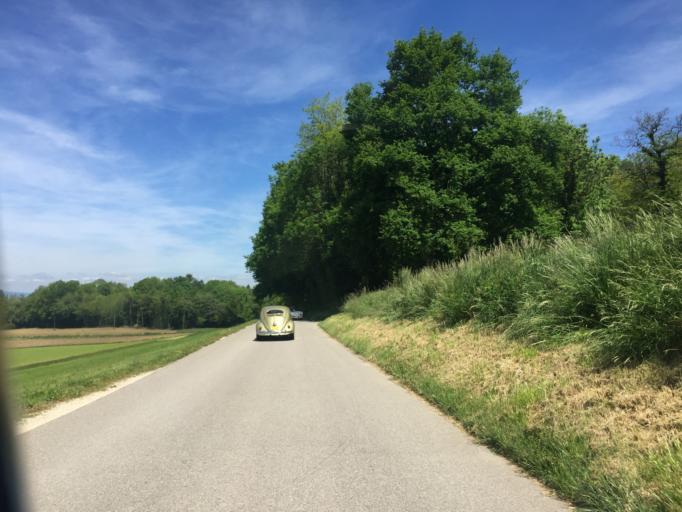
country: FR
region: Rhone-Alpes
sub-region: Departement de la Haute-Savoie
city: Versonnex
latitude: 45.9355
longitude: 5.9695
